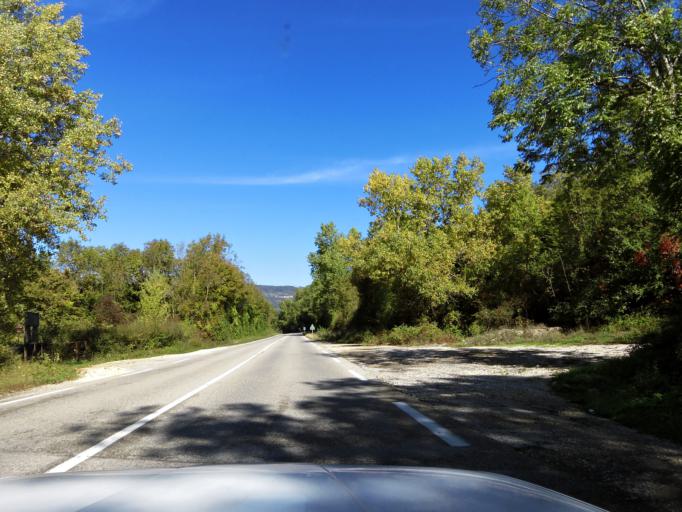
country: FR
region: Rhone-Alpes
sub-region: Departement de l'Isere
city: Porcieu-Amblagnieu
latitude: 45.8335
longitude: 5.4111
